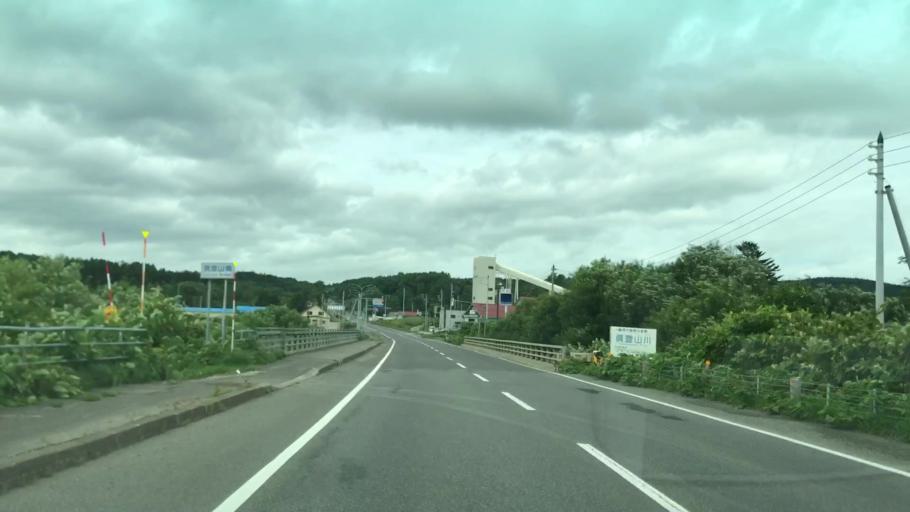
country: JP
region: Hokkaido
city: Niseko Town
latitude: 42.9193
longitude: 140.7440
